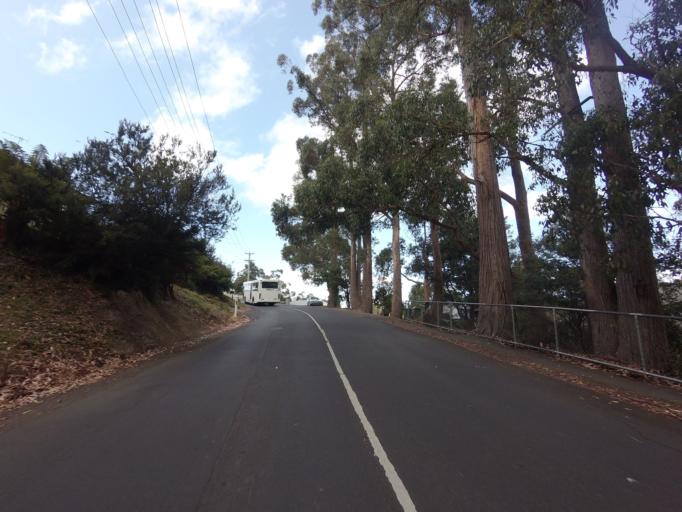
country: AU
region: Tasmania
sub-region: Hobart
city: Dynnyrne
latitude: -42.9006
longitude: 147.2749
